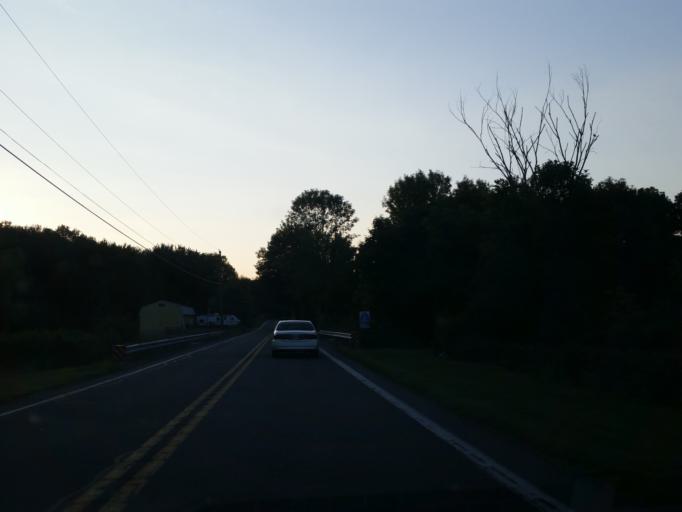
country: US
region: Pennsylvania
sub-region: Lebanon County
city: Newmanstown
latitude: 40.2971
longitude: -76.2436
